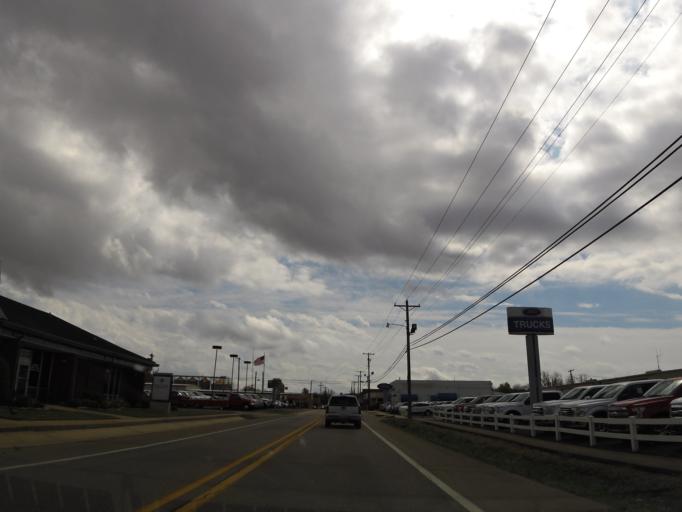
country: US
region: Arkansas
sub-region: Clay County
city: Corning
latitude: 36.4092
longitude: -90.5828
